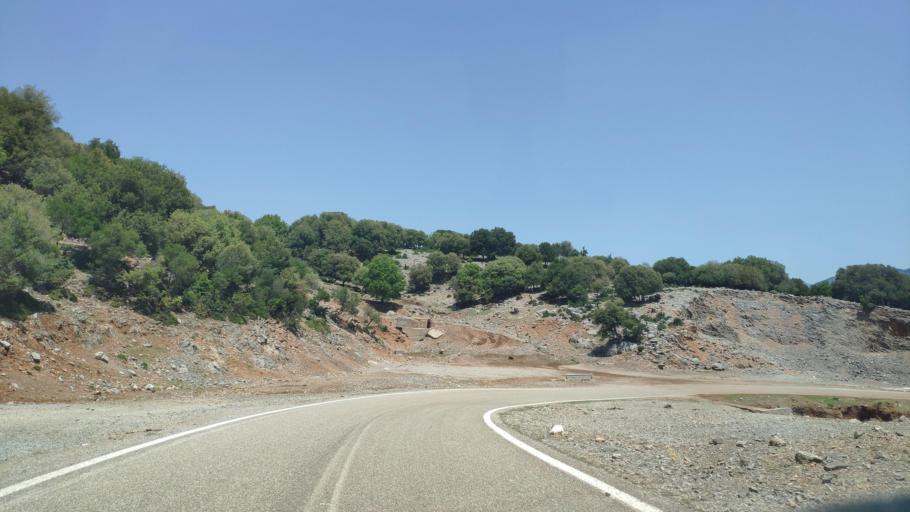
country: GR
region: Central Greece
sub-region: Nomos Evrytanias
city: Kerasochori
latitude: 39.0830
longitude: 21.4105
